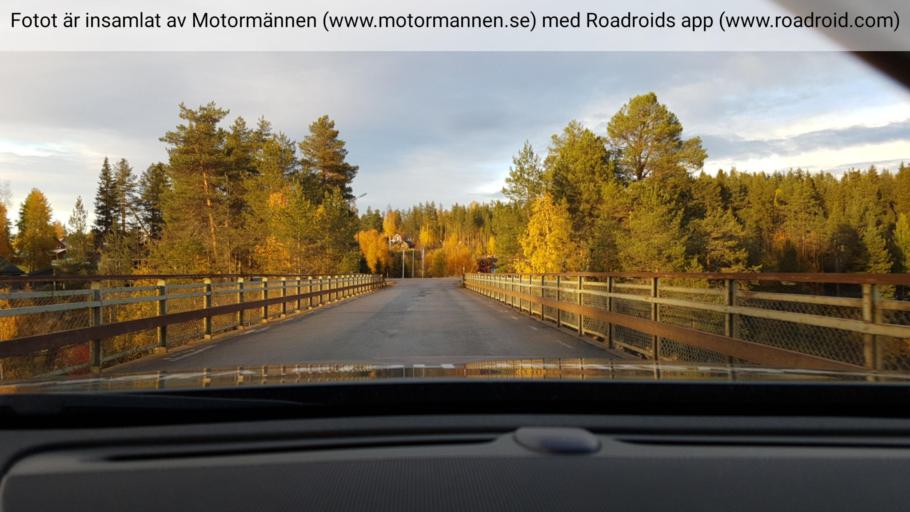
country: SE
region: Norrbotten
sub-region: Overkalix Kommun
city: OEverkalix
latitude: 66.6509
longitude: 22.7123
